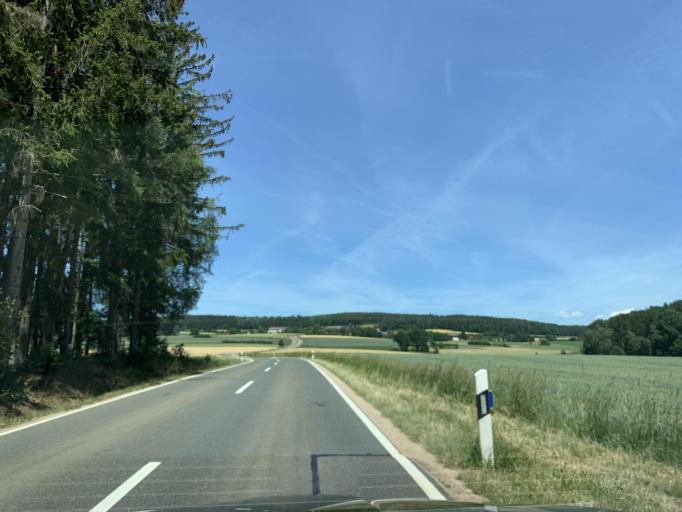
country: DE
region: Bavaria
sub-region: Upper Palatinate
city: Bach
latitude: 49.4011
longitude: 12.3591
